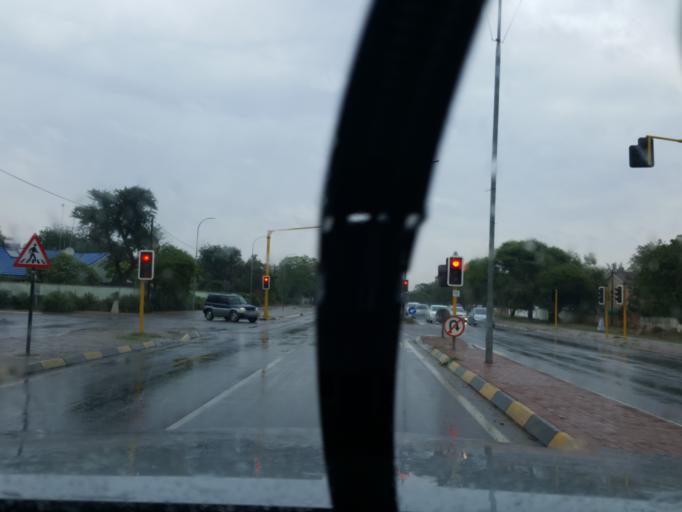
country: BW
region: South East
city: Gaborone
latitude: -24.6437
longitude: 25.9256
